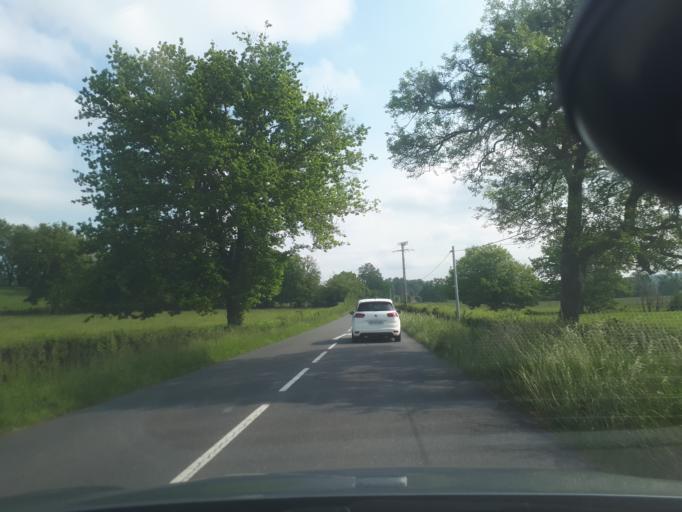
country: FR
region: Auvergne
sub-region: Departement de l'Allier
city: Dompierre-sur-Besbre
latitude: 46.4074
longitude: 3.6031
